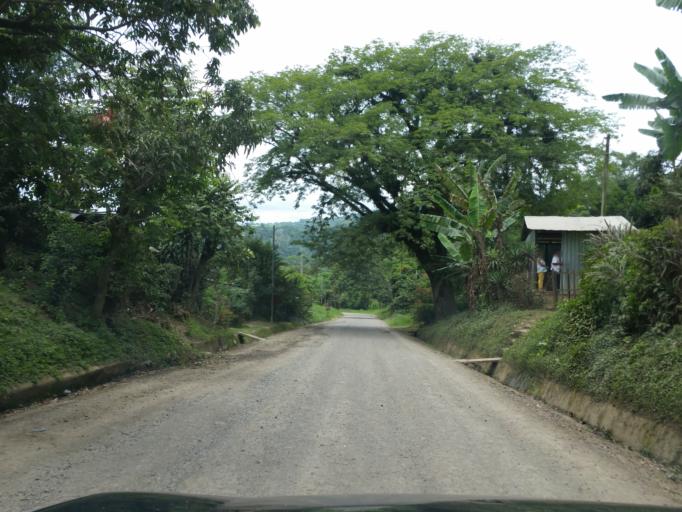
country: NI
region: Matagalpa
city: San Ramon
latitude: 12.9366
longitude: -85.8641
